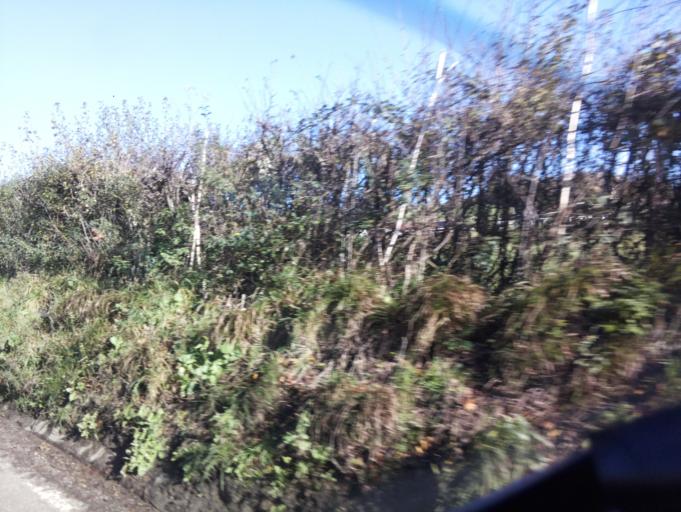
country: GB
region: England
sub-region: Somerset
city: Langport
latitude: 51.0489
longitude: -2.8272
